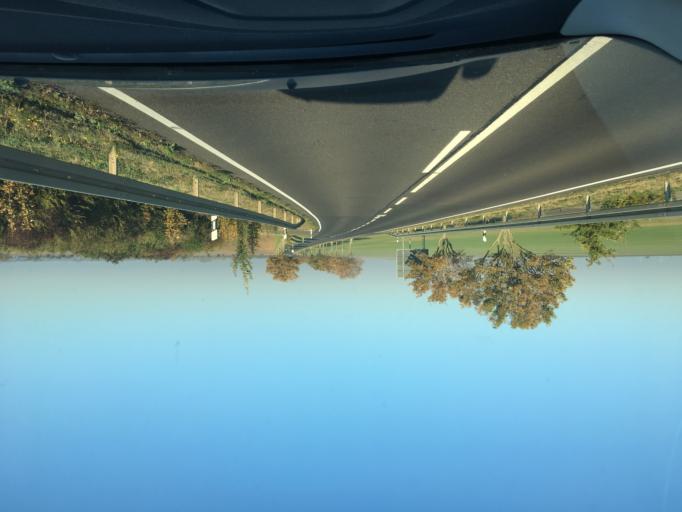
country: DE
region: Saxony-Anhalt
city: Wolmirsleben
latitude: 52.0159
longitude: 11.5051
